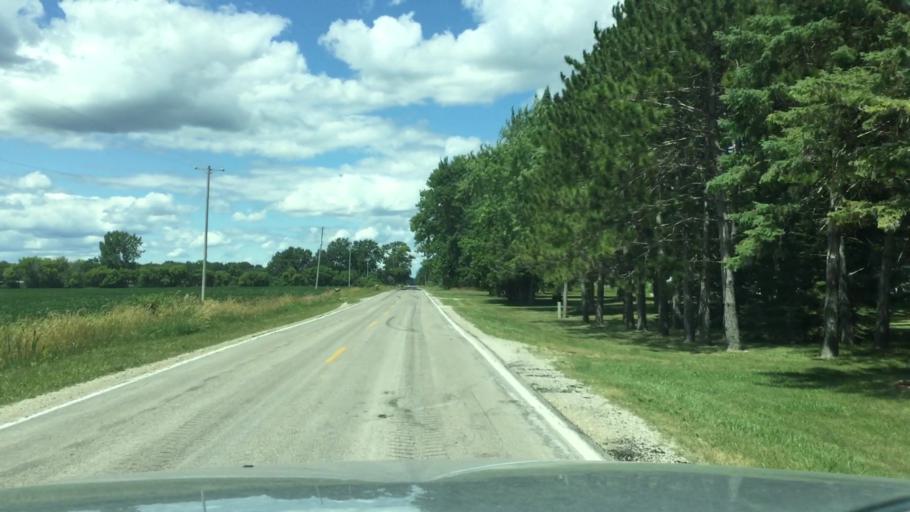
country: US
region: Michigan
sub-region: Saginaw County
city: Saint Charles
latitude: 43.3422
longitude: -84.1899
